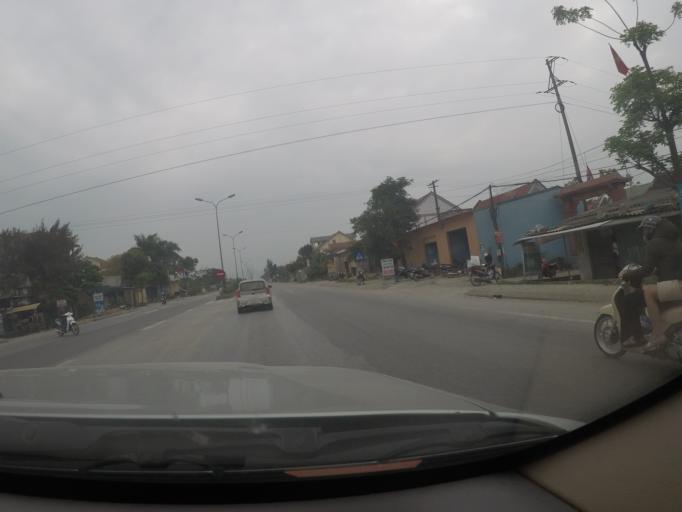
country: VN
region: Nghe An
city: Dien Chau
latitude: 18.9557
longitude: 105.6022
